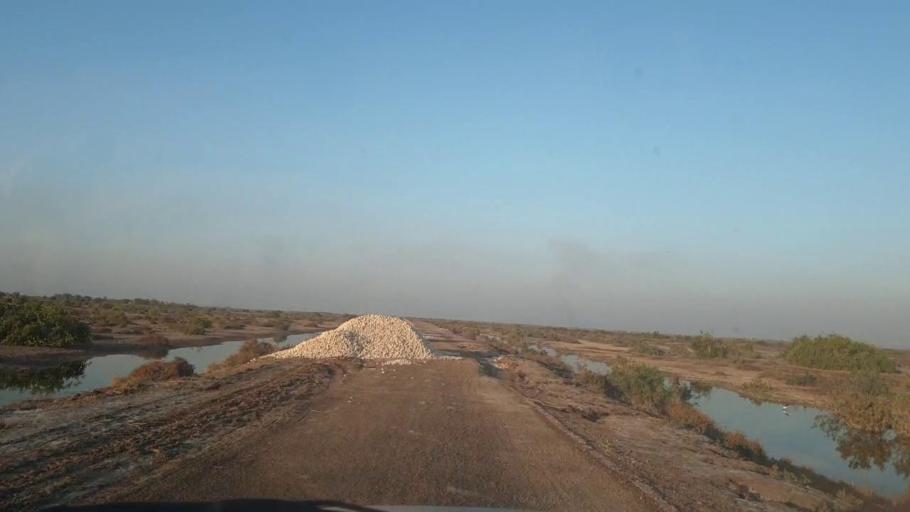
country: PK
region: Sindh
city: Mirpur Khas
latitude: 25.4367
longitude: 69.0765
